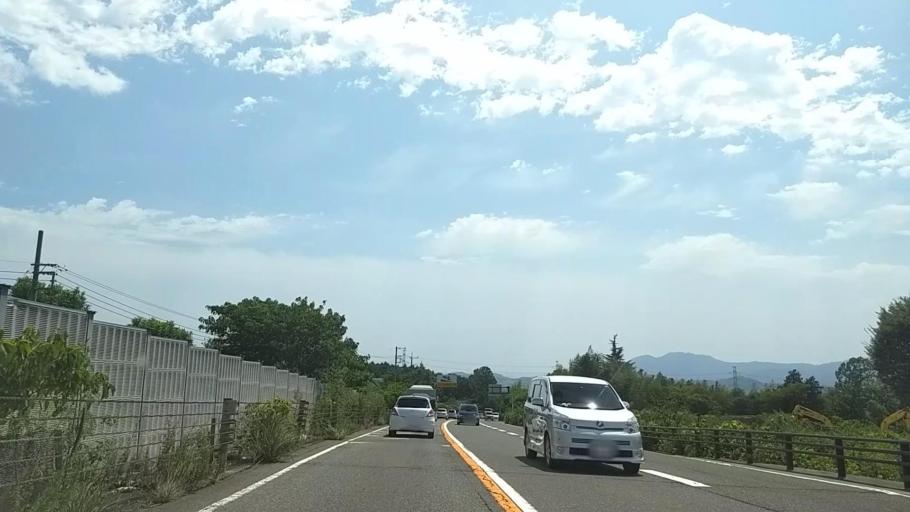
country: JP
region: Shizuoka
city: Fujinomiya
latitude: 35.2690
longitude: 138.6148
